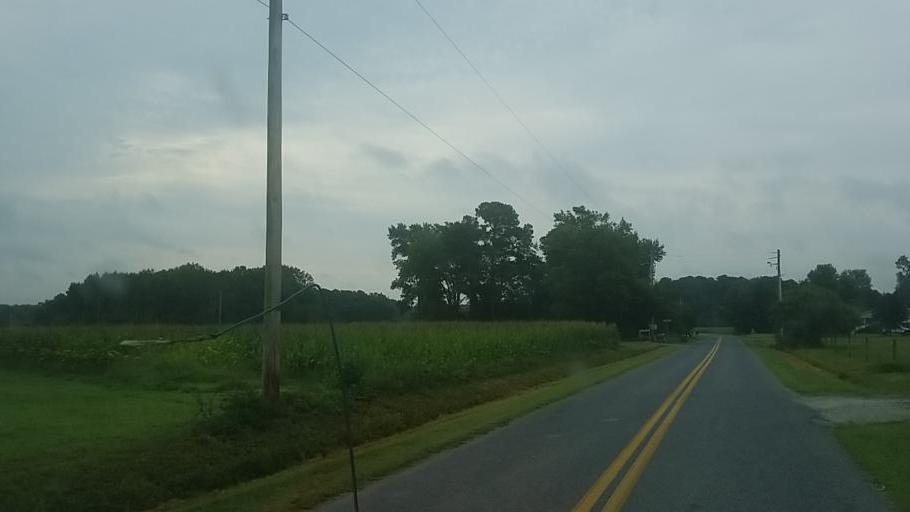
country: US
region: Delaware
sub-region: Sussex County
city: Selbyville
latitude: 38.4279
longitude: -75.1951
